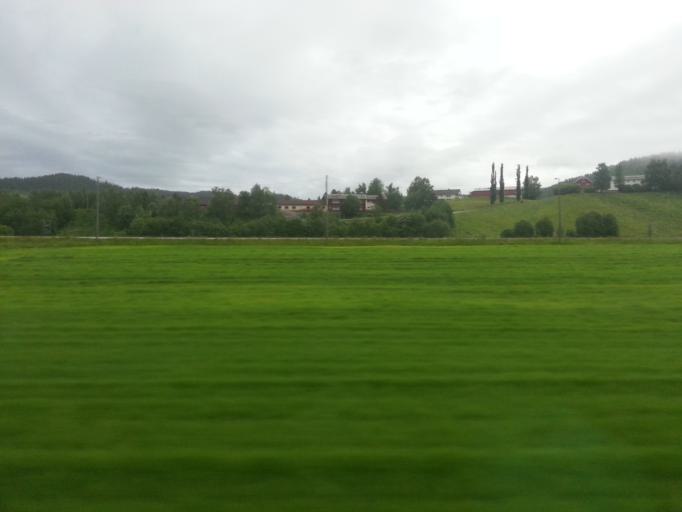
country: NO
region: Sor-Trondelag
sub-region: Melhus
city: Lundamo
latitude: 63.1358
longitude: 10.2505
